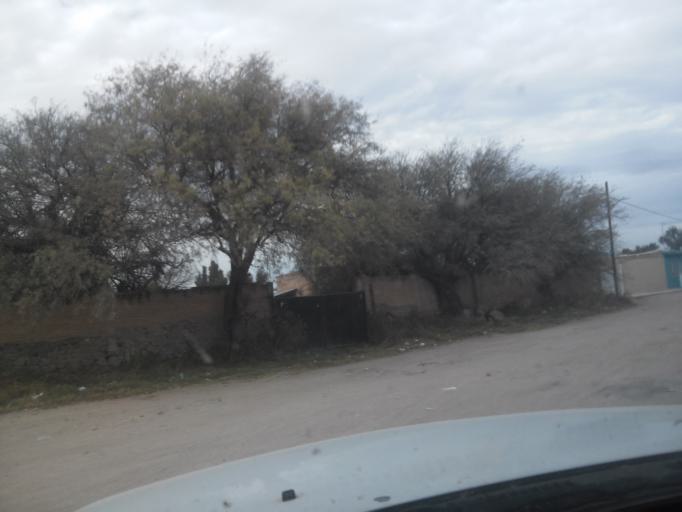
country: MX
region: Durango
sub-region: Durango
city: Jose Refugio Salcido
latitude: 24.0495
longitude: -104.5493
